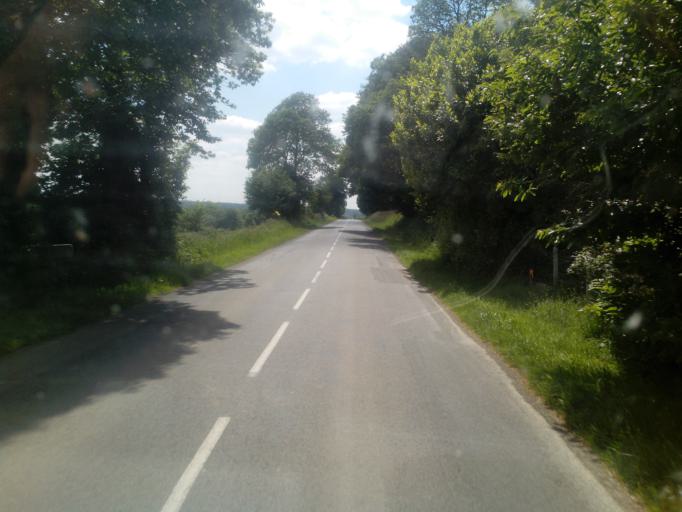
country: FR
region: Brittany
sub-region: Departement d'Ille-et-Vilaine
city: Montreuil-sur-Ille
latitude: 48.3150
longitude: -1.6567
